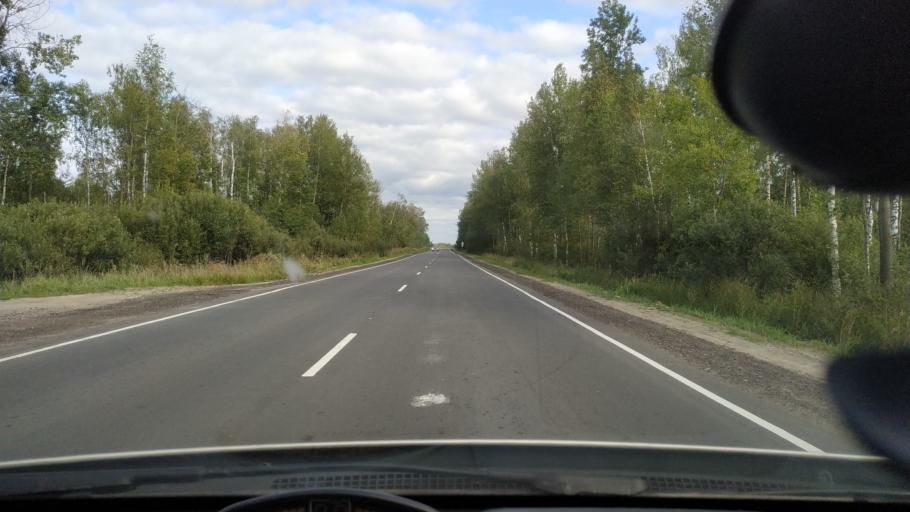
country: RU
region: Moskovskaya
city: Vereya
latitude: 55.7265
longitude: 39.0374
